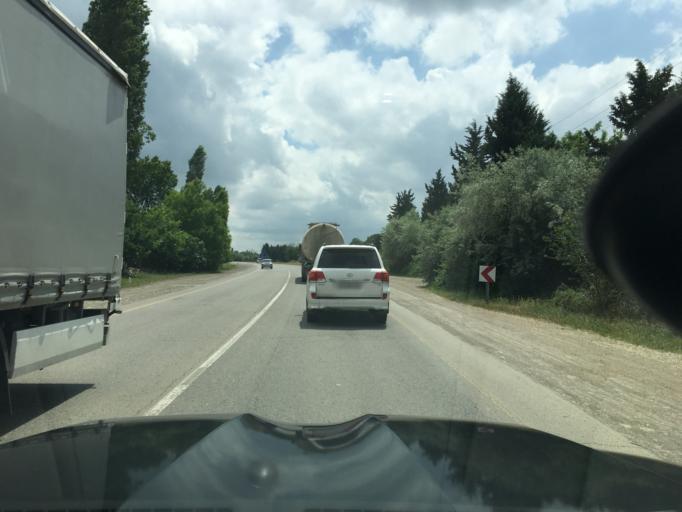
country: AZ
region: Tovuz
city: Qaraxanli
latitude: 41.0317
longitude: 45.5948
